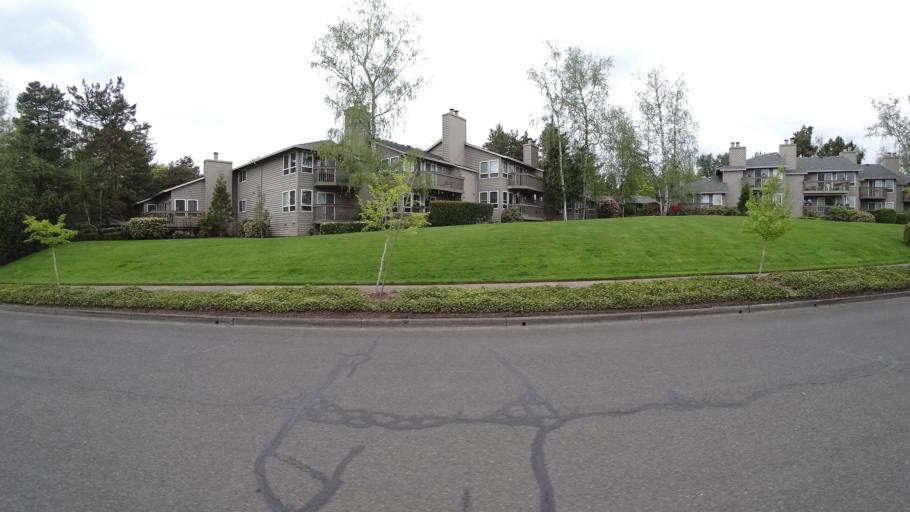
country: US
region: Oregon
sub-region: Washington County
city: Beaverton
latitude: 45.4560
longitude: -122.8238
